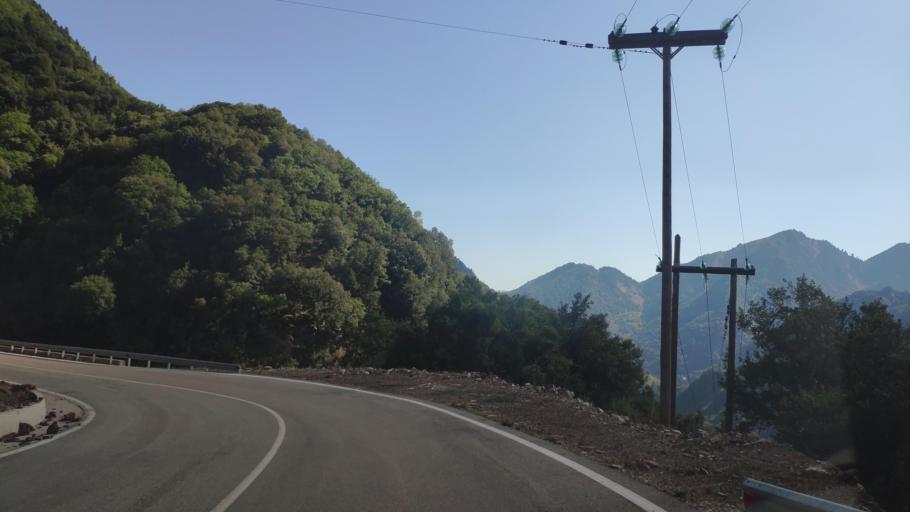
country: GR
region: Central Greece
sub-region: Nomos Evrytanias
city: Kerasochori
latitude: 39.1034
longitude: 21.6097
